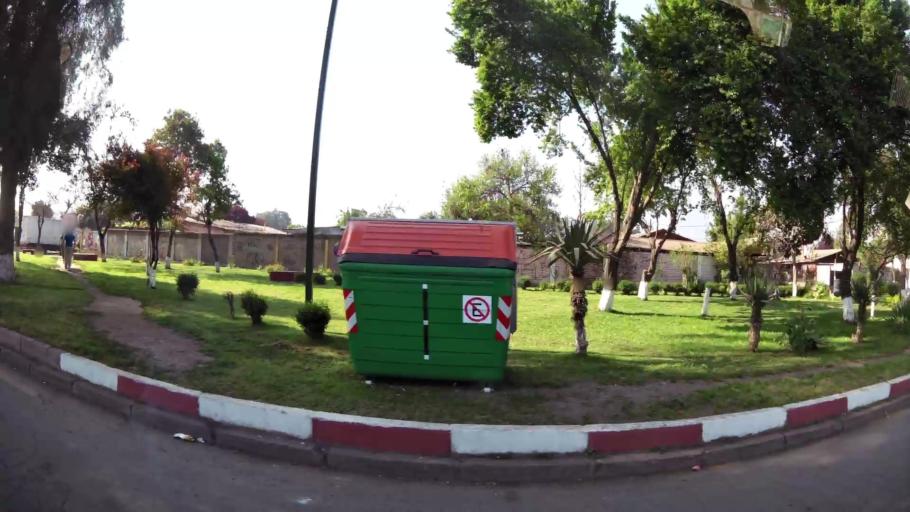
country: CL
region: Santiago Metropolitan
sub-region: Provincia de Santiago
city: Lo Prado
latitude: -33.3710
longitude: -70.6768
